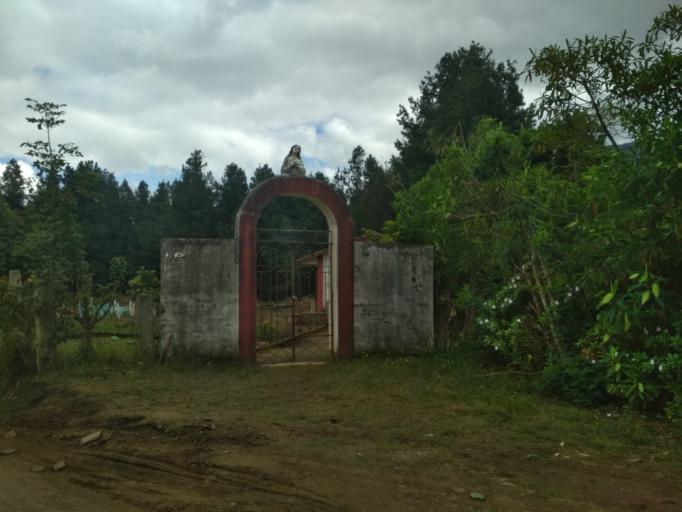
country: CO
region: Cauca
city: Jambalo
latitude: 2.7149
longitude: -76.3237
